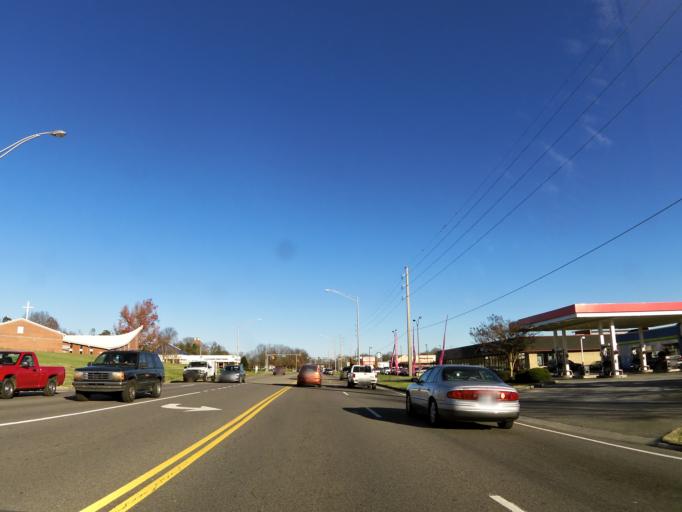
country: US
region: Tennessee
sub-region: Anderson County
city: Oak Ridge
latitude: 36.0144
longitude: -84.2572
